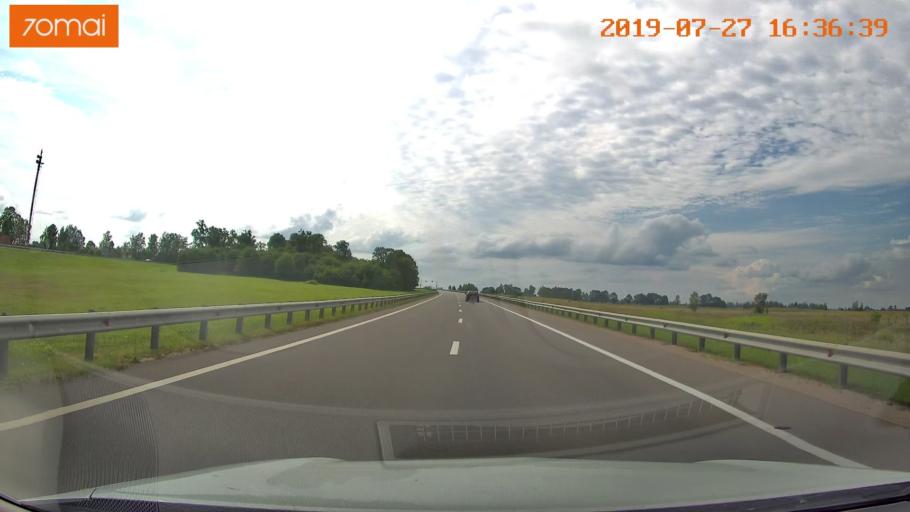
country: RU
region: Kaliningrad
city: Gvardeysk
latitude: 54.6486
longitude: 21.2781
